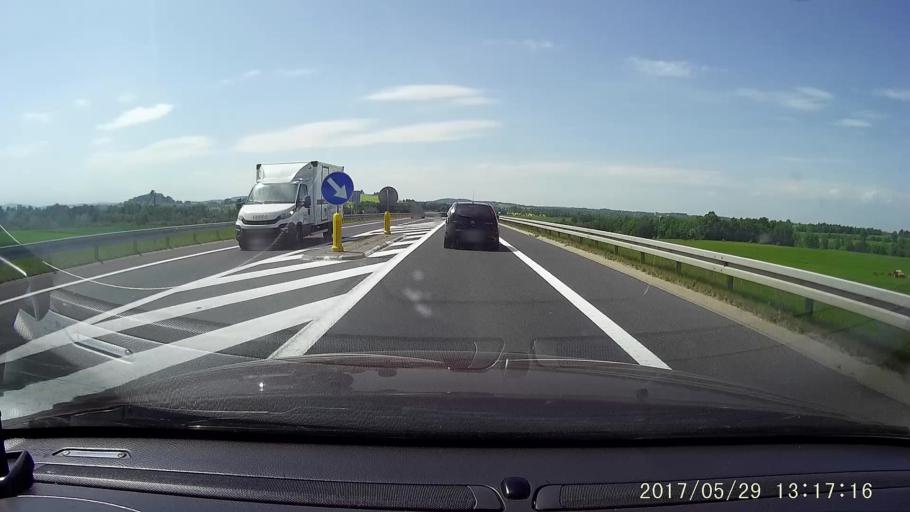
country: PL
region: Lower Silesian Voivodeship
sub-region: Powiat lwowecki
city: Lubomierz
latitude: 51.0009
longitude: 15.4646
